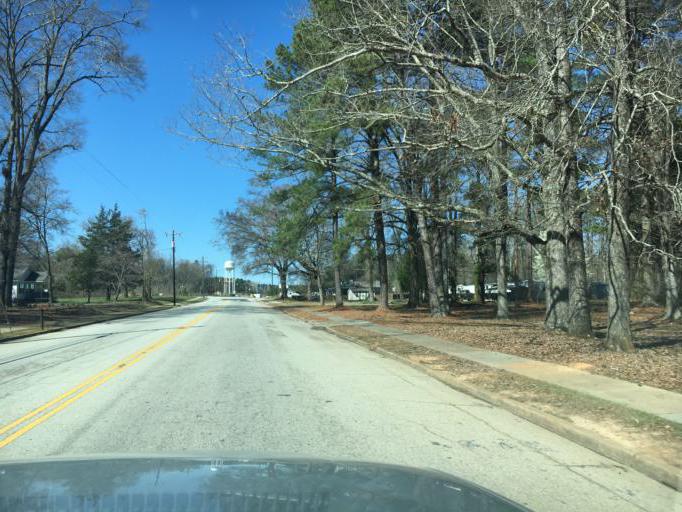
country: US
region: South Carolina
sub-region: Greenwood County
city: Ninety Six
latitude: 34.3132
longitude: -81.9894
